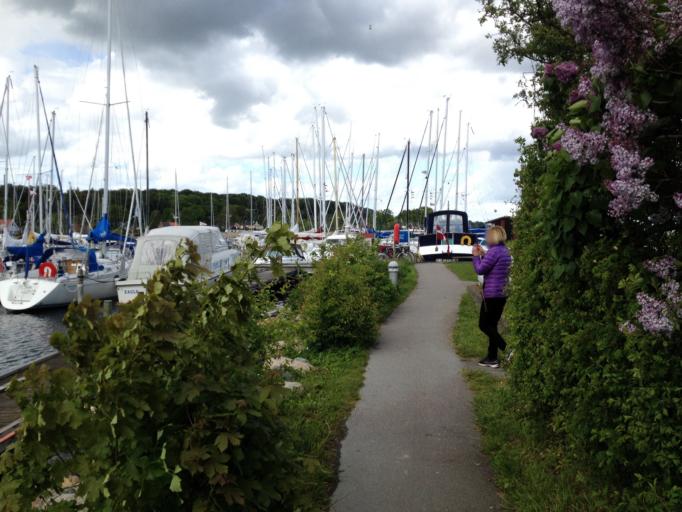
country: DK
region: Capital Region
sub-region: Fredensborg Kommune
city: Niva
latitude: 55.9386
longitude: 12.5267
